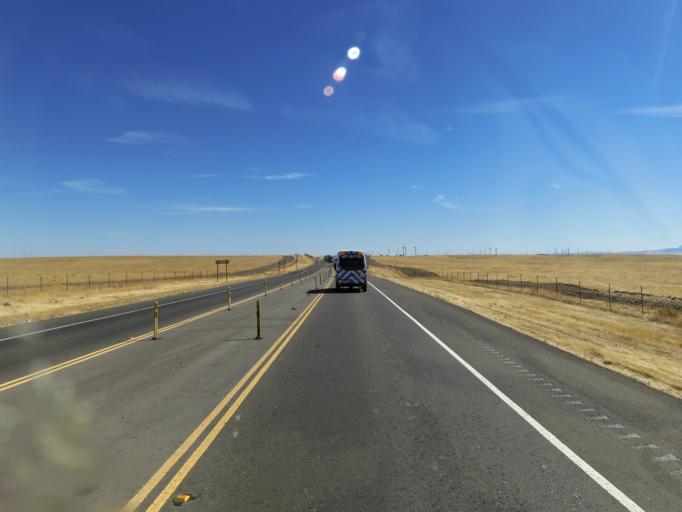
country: US
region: California
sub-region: Solano County
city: Suisun
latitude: 38.2194
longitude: -121.8881
